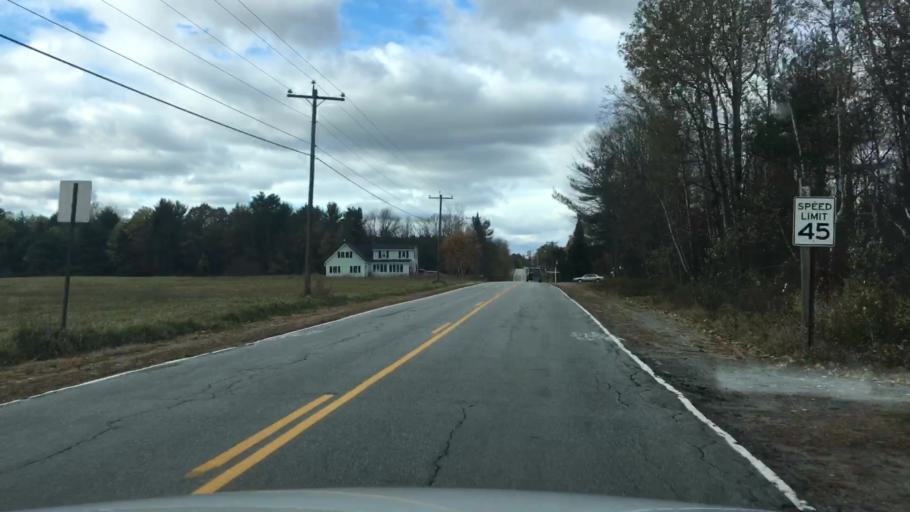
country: US
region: Maine
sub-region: Kennebec County
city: Monmouth
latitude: 44.2095
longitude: -70.0821
